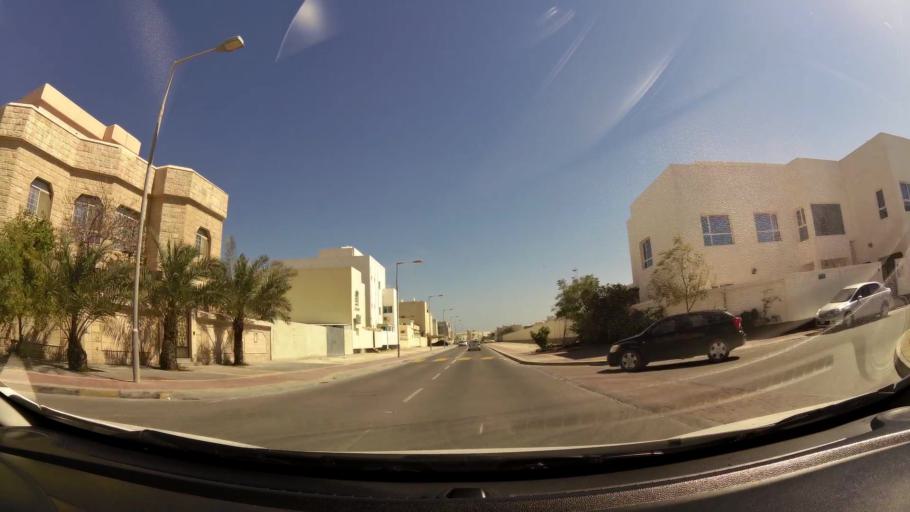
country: BH
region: Muharraq
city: Al Hadd
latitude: 26.2749
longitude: 50.6537
